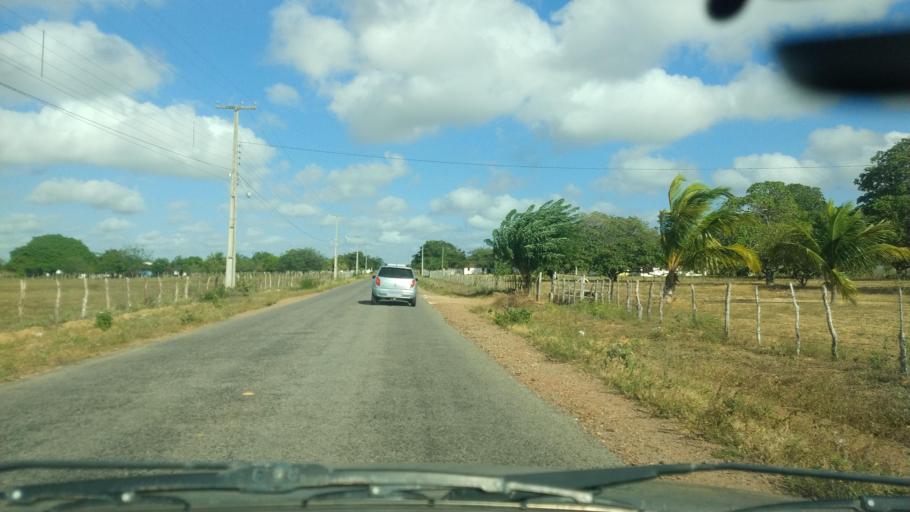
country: BR
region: Rio Grande do Norte
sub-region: Sao Paulo Do Potengi
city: Sao Paulo do Potengi
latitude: -5.9158
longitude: -35.7156
